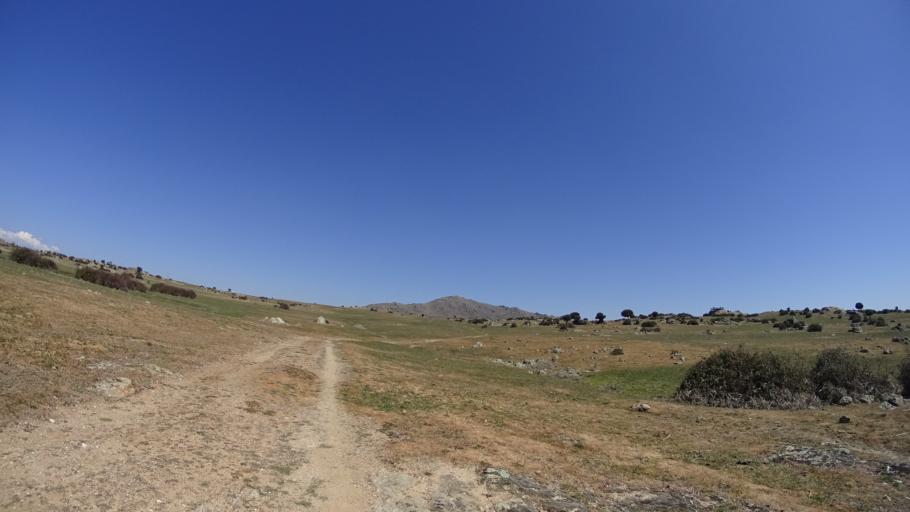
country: ES
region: Madrid
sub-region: Provincia de Madrid
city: Colmenar Viejo
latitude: 40.7059
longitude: -3.7542
